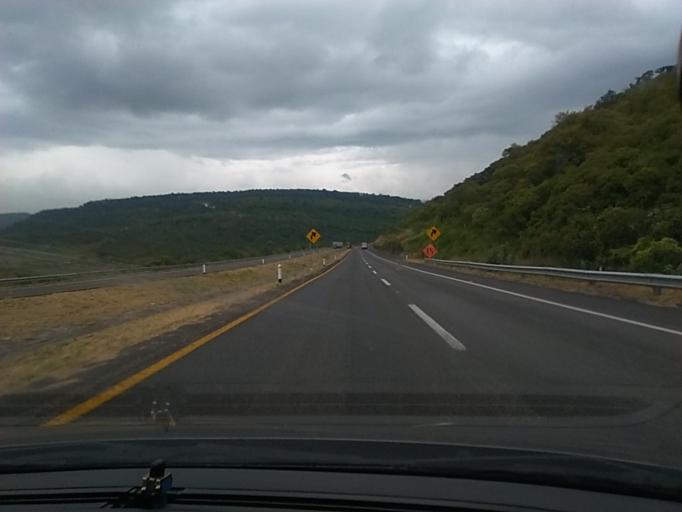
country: MX
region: Jalisco
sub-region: Zapotlan del Rey
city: Zapotlan del Rey
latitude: 20.5002
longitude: -102.9508
